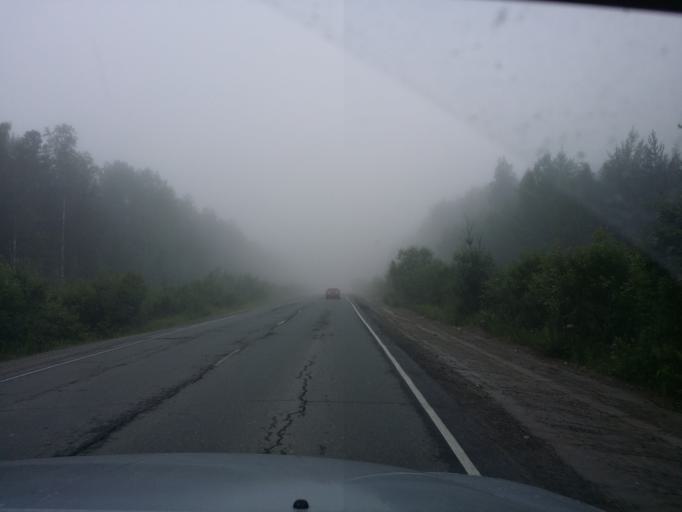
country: RU
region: Khanty-Mansiyskiy Avtonomnyy Okrug
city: Gornopravdinsk
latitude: 59.6373
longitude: 69.8197
